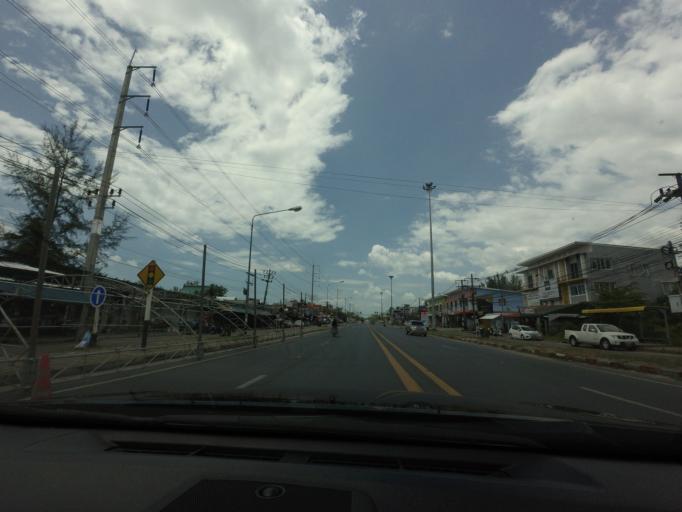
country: TH
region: Phangnga
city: Ban Khao Lak
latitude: 8.6659
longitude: 98.2531
